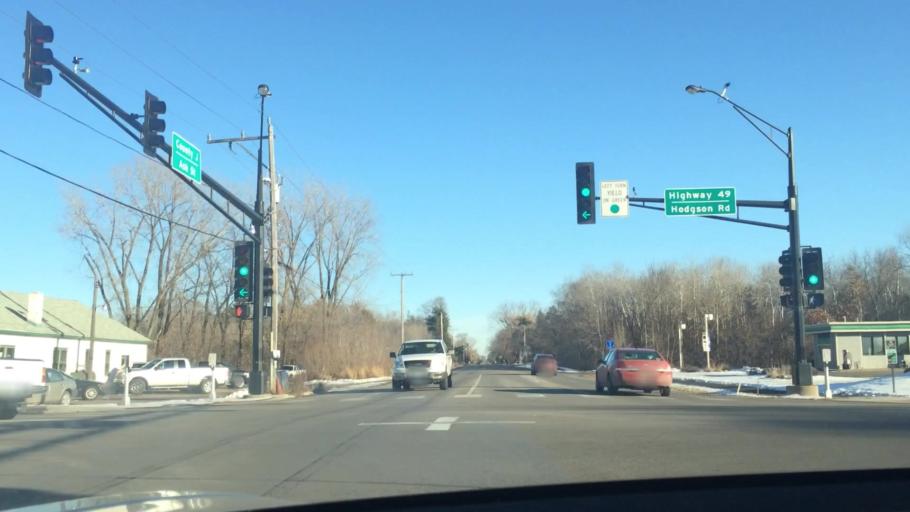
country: US
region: Minnesota
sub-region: Anoka County
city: Circle Pines
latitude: 45.1241
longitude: -93.1276
